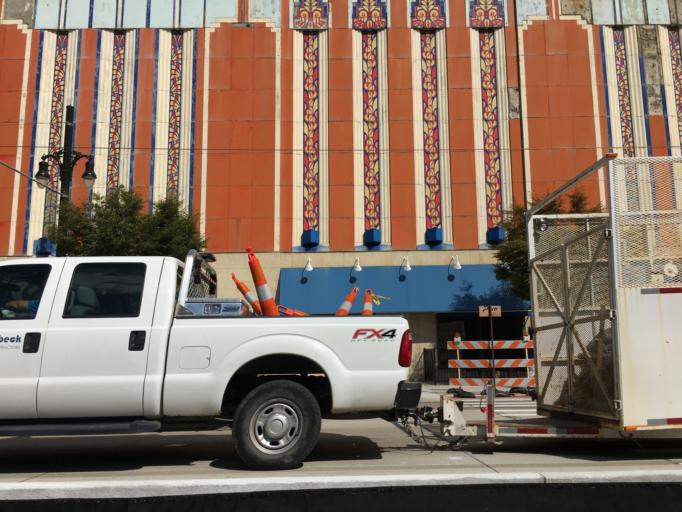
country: US
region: Michigan
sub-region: Wayne County
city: Detroit
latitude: 42.3514
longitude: -83.0606
